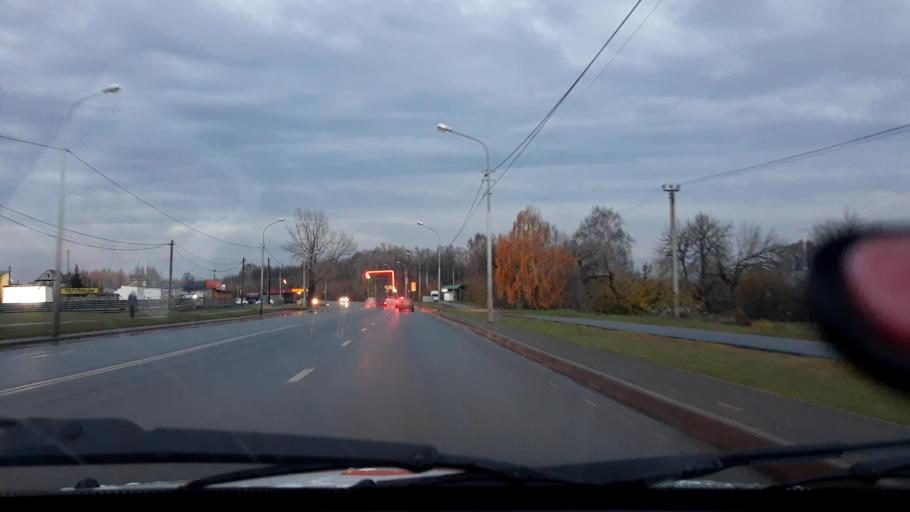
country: RU
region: Bashkortostan
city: Iglino
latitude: 54.7791
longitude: 56.2282
